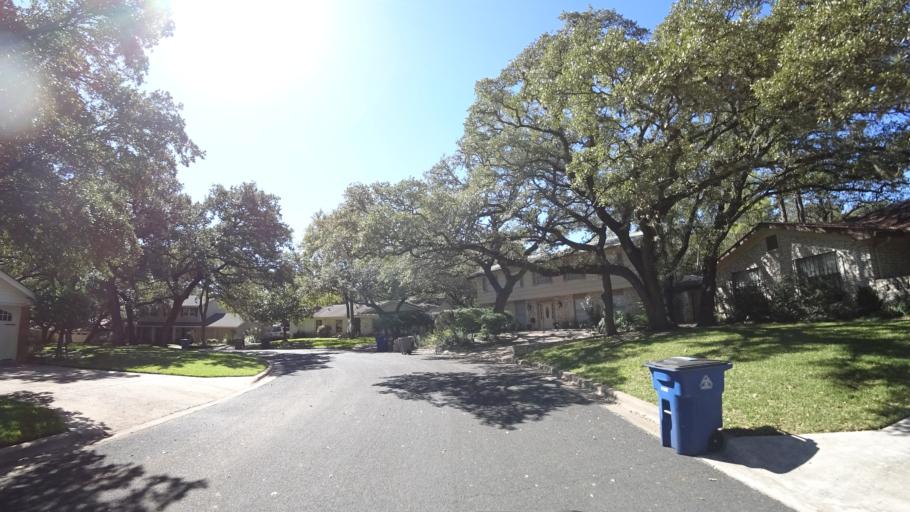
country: US
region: Texas
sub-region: Travis County
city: West Lake Hills
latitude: 30.3635
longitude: -97.7659
